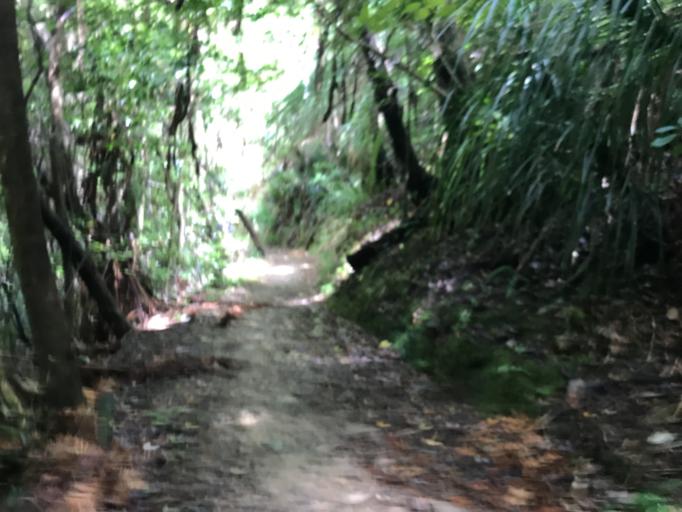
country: NZ
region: Marlborough
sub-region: Marlborough District
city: Picton
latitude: -41.2474
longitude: 173.9550
